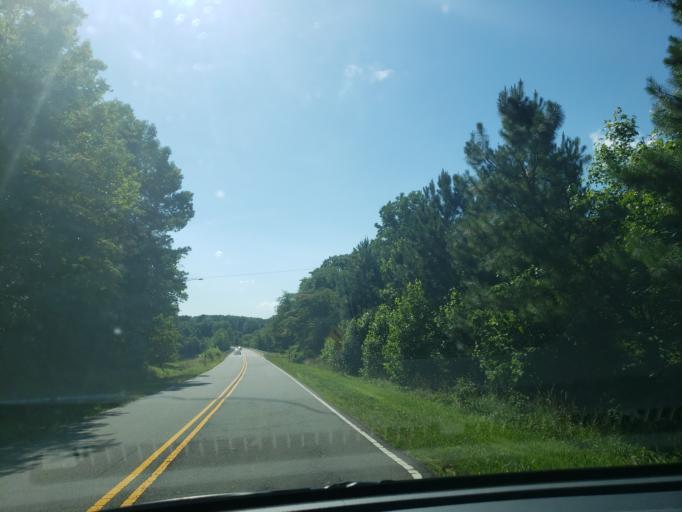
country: US
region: North Carolina
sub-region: Durham County
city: Gorman
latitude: 36.1276
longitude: -78.8717
